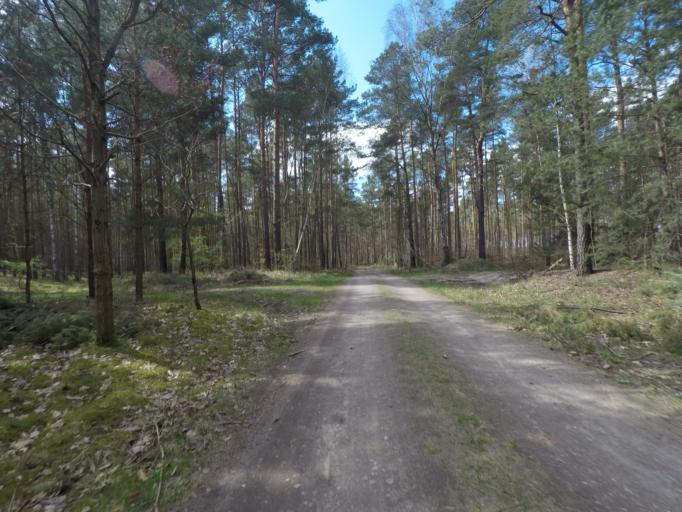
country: DE
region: Brandenburg
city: Melchow
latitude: 52.8160
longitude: 13.7019
